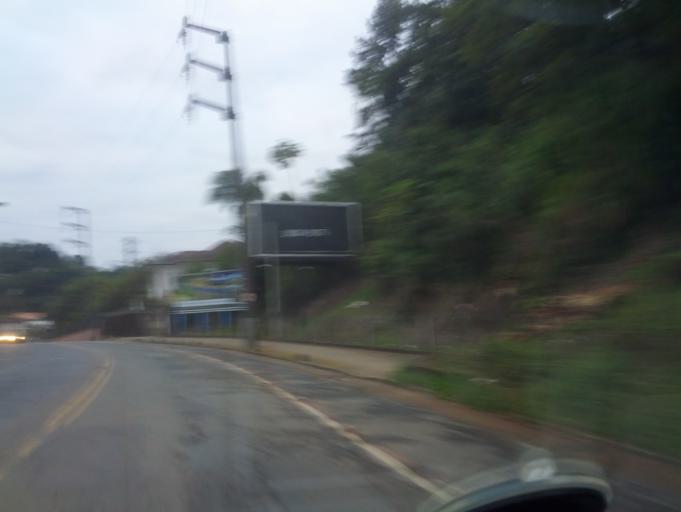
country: BR
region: Santa Catarina
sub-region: Blumenau
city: Blumenau
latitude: -26.8988
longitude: -49.0875
